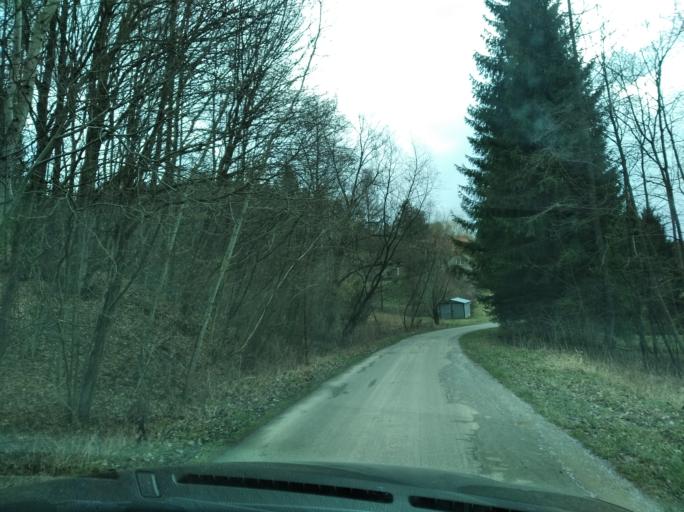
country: PL
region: Subcarpathian Voivodeship
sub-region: Powiat strzyzowski
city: Konieczkowa
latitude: 49.8306
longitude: 21.9376
